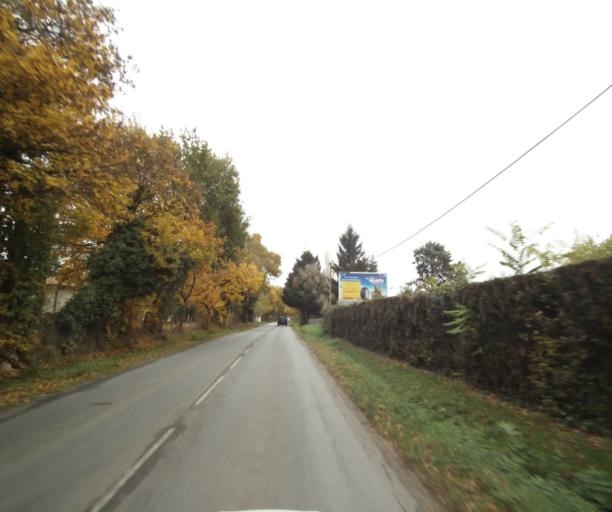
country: FR
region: Poitou-Charentes
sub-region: Departement de la Charente-Maritime
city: Saintes
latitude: 45.7641
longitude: -0.6407
